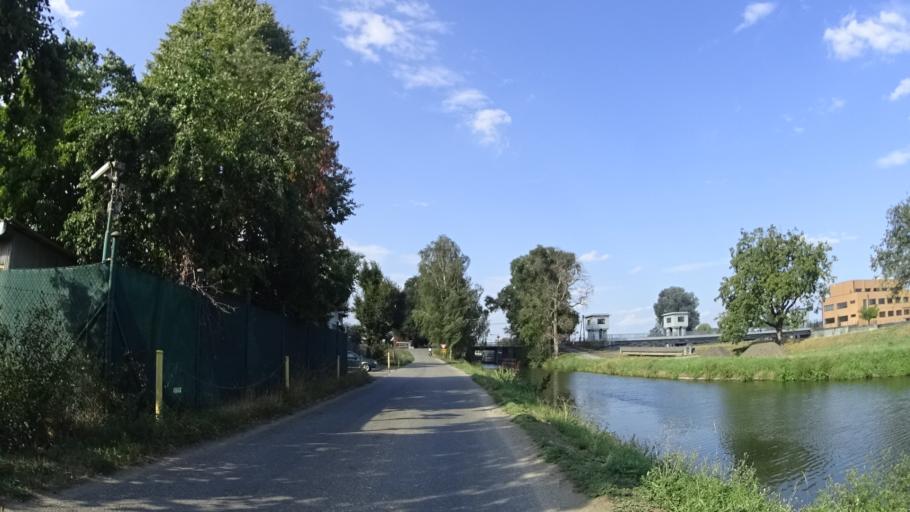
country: CZ
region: Zlin
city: Spytihnev
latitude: 49.1344
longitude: 17.5008
